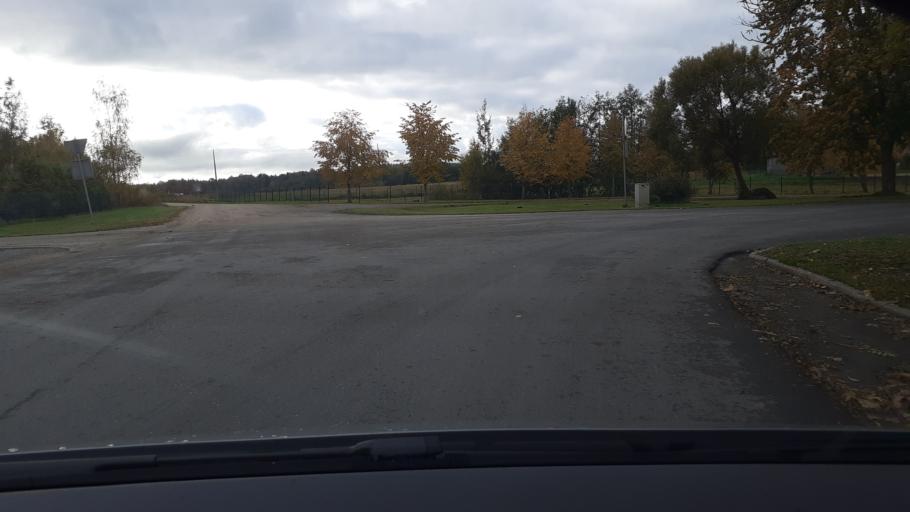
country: LV
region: Kuldigas Rajons
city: Kuldiga
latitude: 57.0167
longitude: 21.9131
